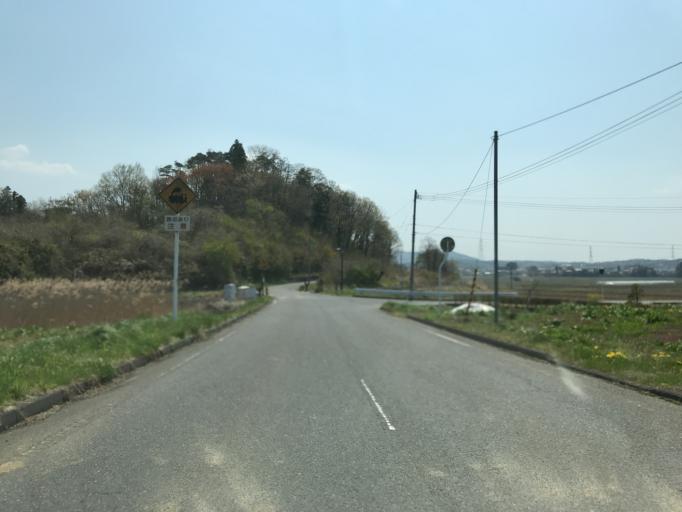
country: JP
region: Fukushima
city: Ishikawa
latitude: 37.0954
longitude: 140.4092
